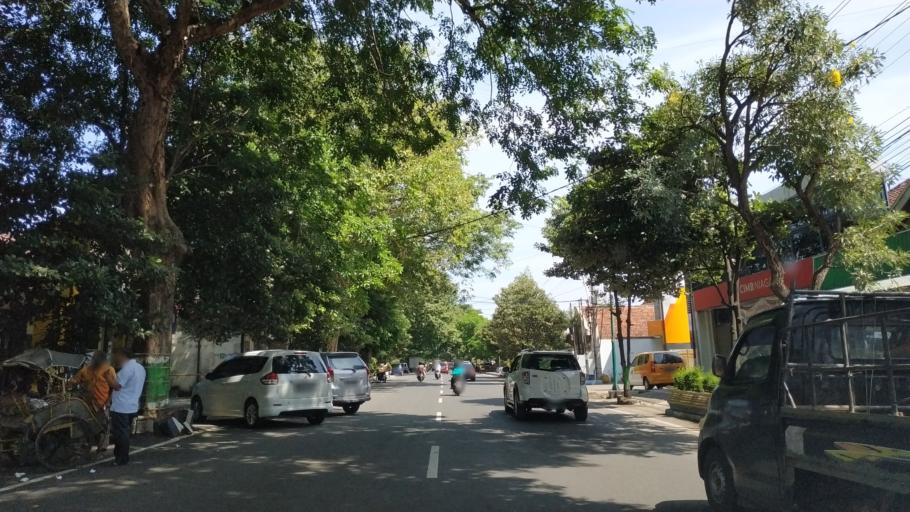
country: ID
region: Central Java
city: Pati
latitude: -6.7520
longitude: 111.0350
